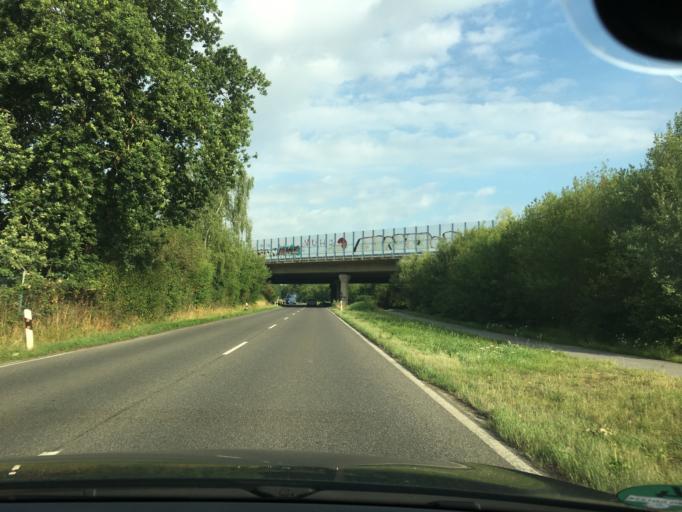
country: DE
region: North Rhine-Westphalia
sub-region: Regierungsbezirk Koln
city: Niederzier
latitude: 50.8350
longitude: 6.4387
